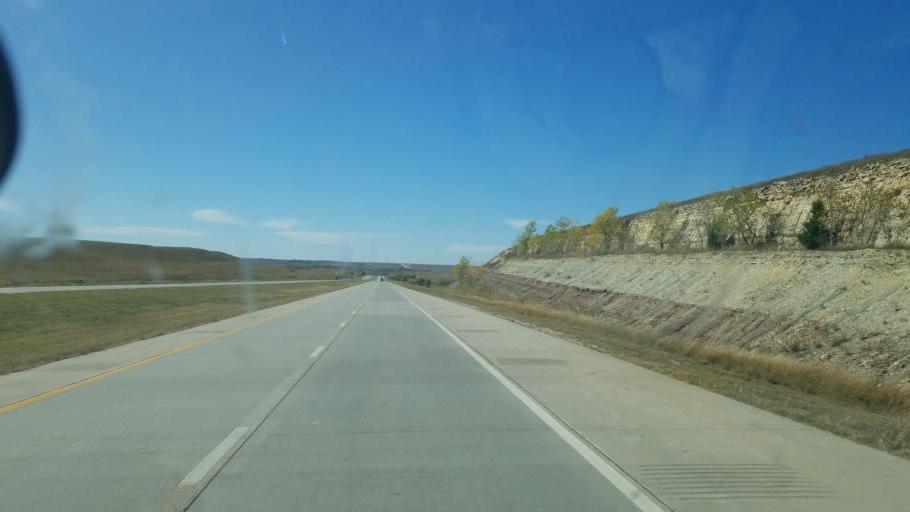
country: US
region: Kansas
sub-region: Riley County
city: Manhattan
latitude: 39.0665
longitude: -96.5883
